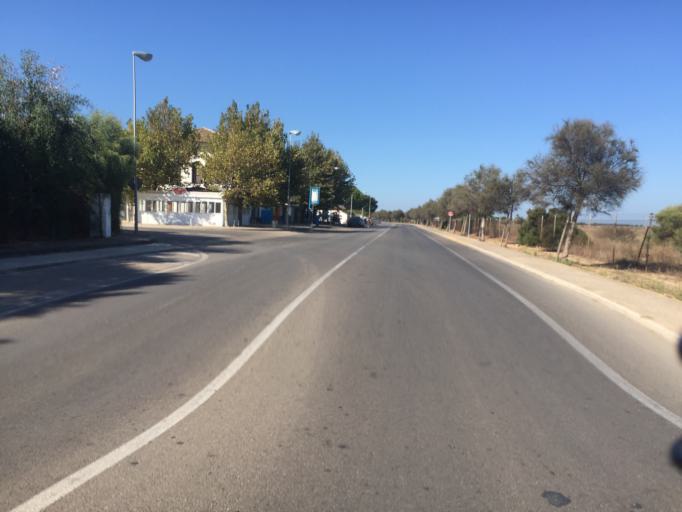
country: ES
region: Andalusia
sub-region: Provincia de Cadiz
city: Chiclana de la Frontera
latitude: 36.3844
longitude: -6.1937
